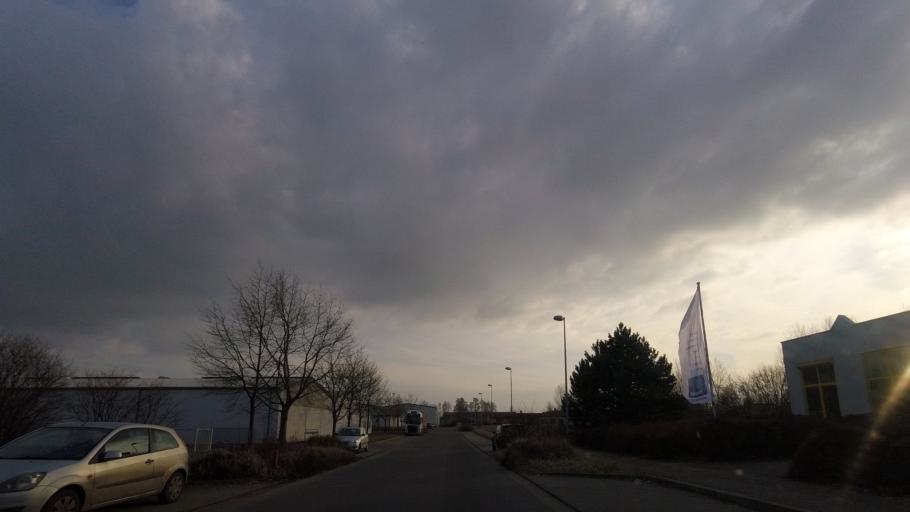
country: DE
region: Brandenburg
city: Wiesenburg
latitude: 52.1168
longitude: 12.4660
